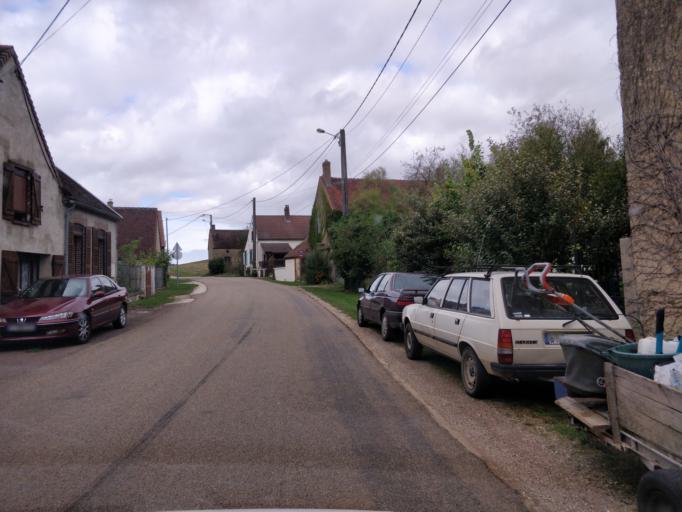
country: FR
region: Champagne-Ardenne
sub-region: Departement de l'Aube
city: Aix-en-Othe
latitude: 48.1685
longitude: 3.6278
